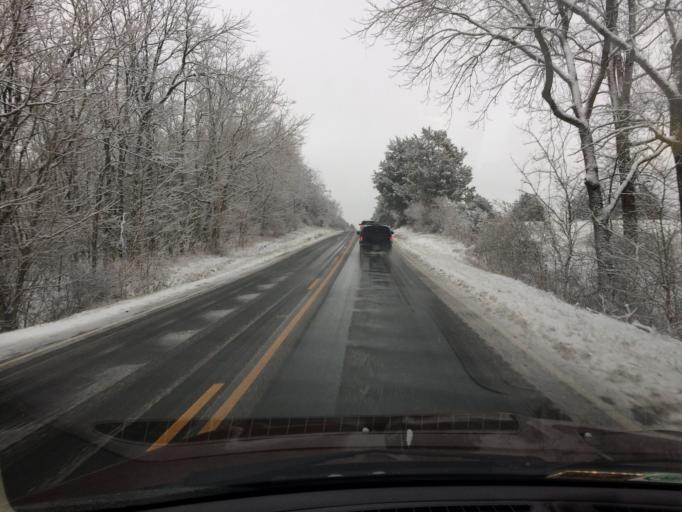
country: US
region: Virginia
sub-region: Amherst County
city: Amherst
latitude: 37.5992
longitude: -79.0609
